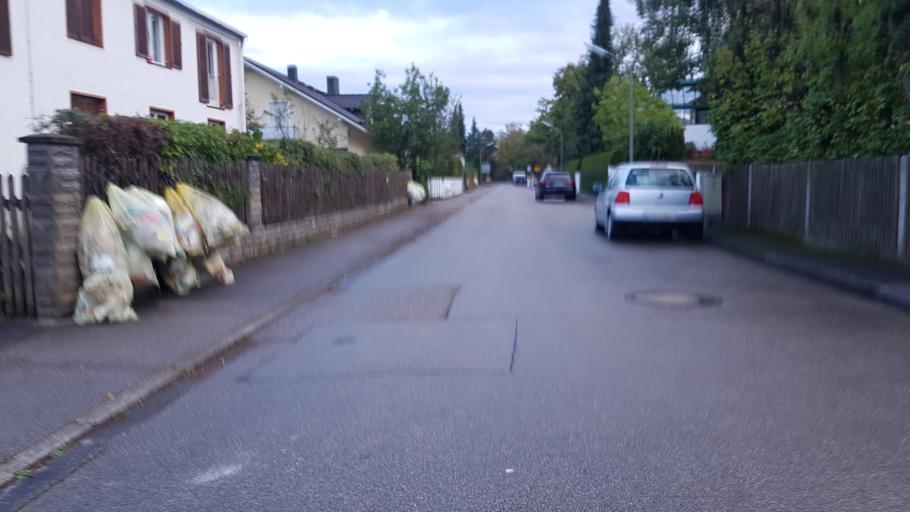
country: DE
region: Bavaria
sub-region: Upper Bavaria
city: Neubiberg
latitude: 48.0777
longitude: 11.6741
